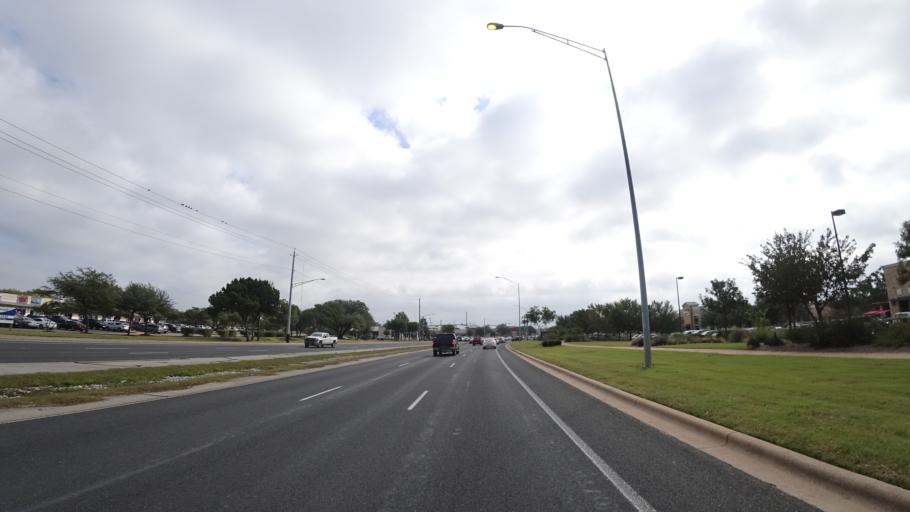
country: US
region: Texas
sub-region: Travis County
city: Shady Hollow
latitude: 30.2230
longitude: -97.8405
